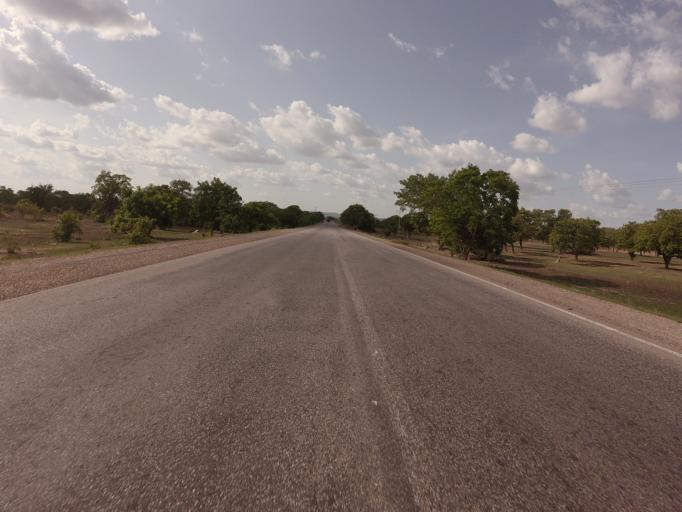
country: GH
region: Upper East
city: Bolgatanga
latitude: 10.5753
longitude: -0.8326
